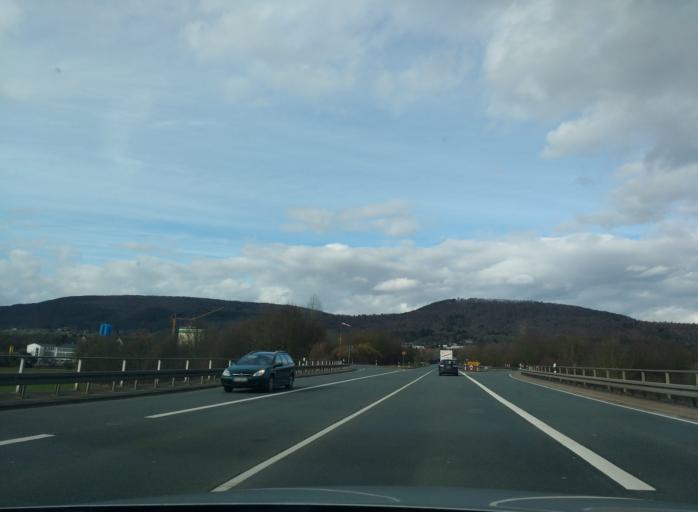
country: DE
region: Lower Saxony
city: Rinteln
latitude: 52.1945
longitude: 9.0951
